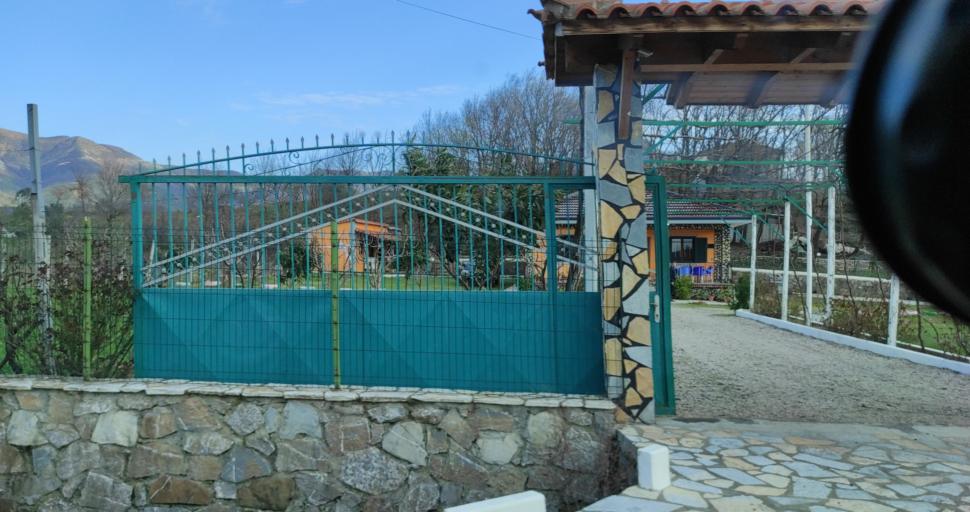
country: AL
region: Lezhe
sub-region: Rrethi i Lezhes
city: Kallmeti i Madh
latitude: 41.8812
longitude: 19.6783
